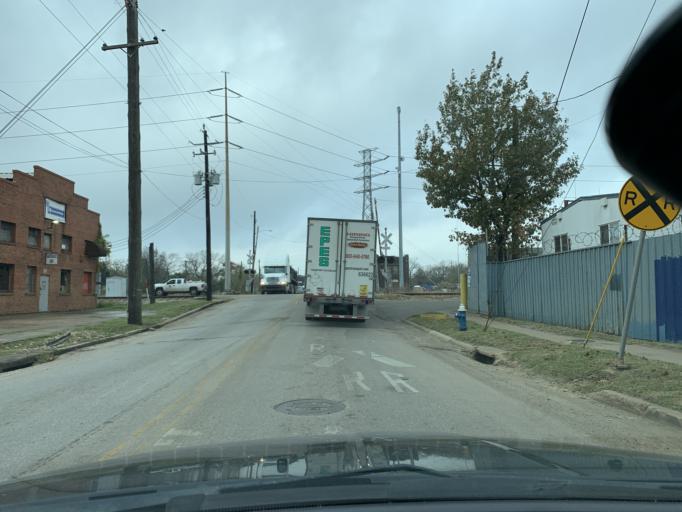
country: US
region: Texas
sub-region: Harris County
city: Houston
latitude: 29.7835
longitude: -95.3482
